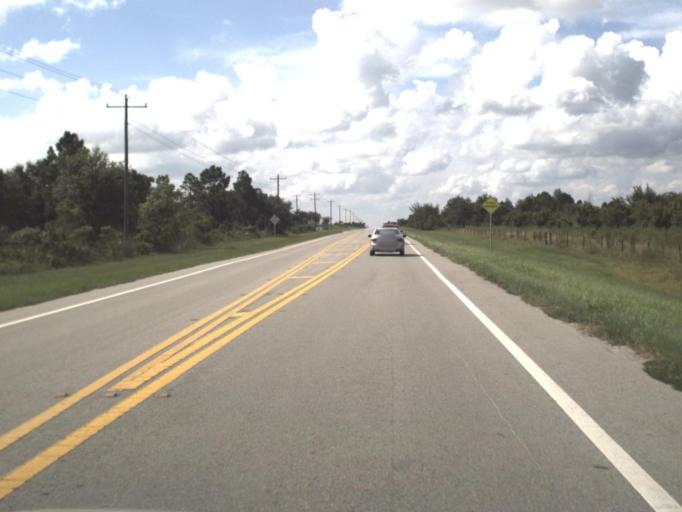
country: US
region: Florida
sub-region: Hillsborough County
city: Wimauma
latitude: 27.4625
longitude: -82.1855
